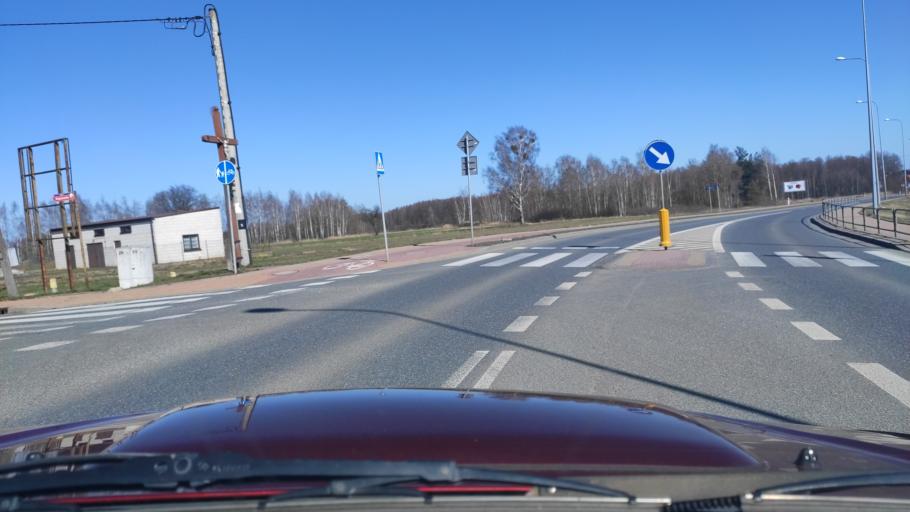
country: PL
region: Masovian Voivodeship
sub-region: Powiat zwolenski
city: Zwolen
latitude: 51.3722
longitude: 21.5871
